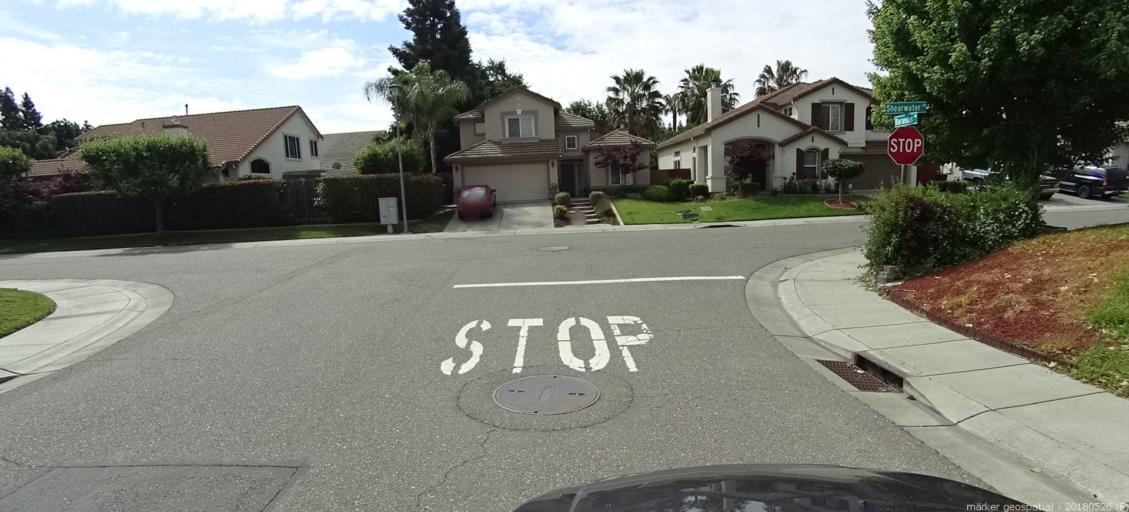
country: US
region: California
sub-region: Yolo County
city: West Sacramento
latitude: 38.6067
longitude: -121.5378
